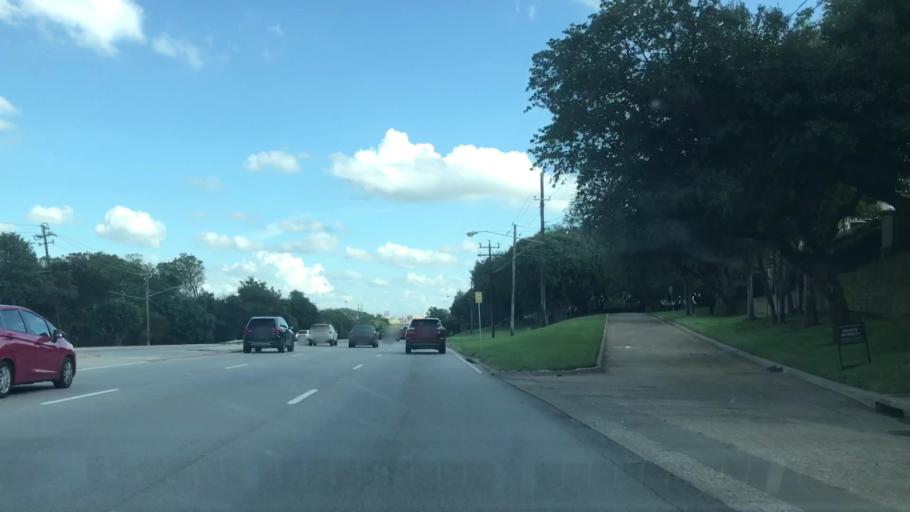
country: US
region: Texas
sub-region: Dallas County
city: University Park
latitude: 32.8638
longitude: -96.7596
